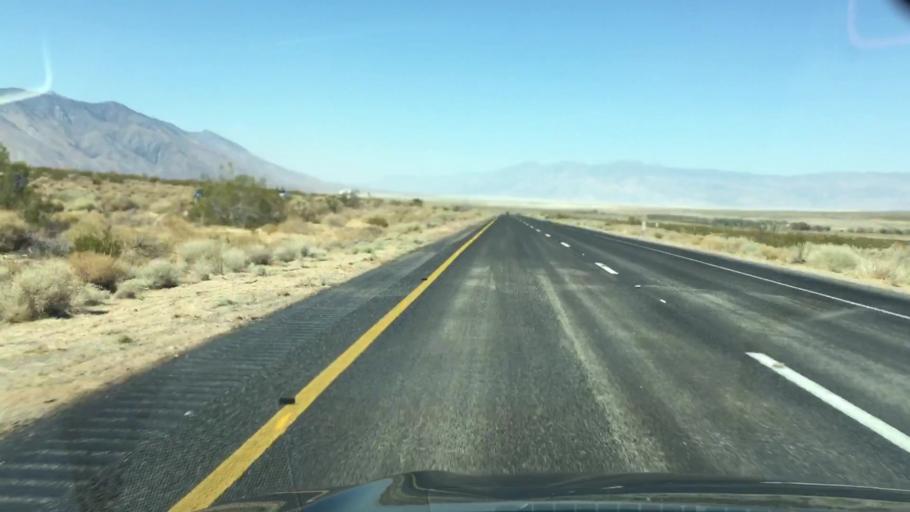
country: US
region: California
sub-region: Inyo County
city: Lone Pine
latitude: 36.2178
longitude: -117.9797
